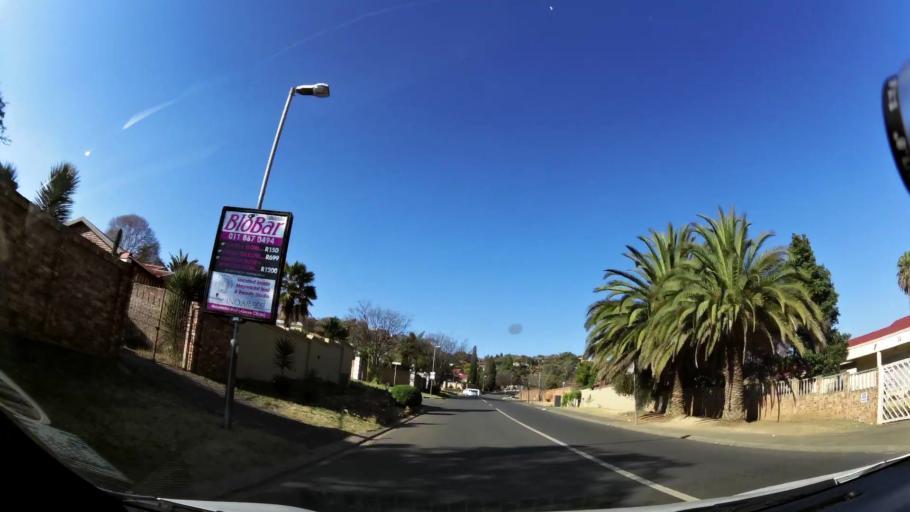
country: ZA
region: Gauteng
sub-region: City of Johannesburg Metropolitan Municipality
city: Johannesburg
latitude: -26.2903
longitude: 28.0528
